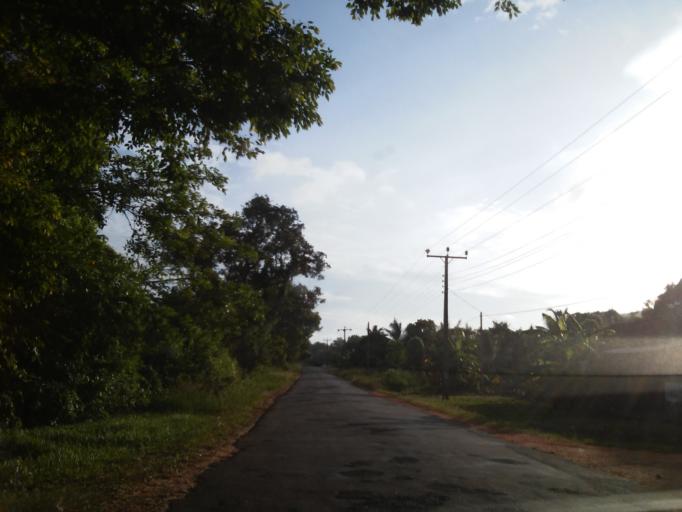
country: LK
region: Central
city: Sigiriya
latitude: 8.1494
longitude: 80.6465
